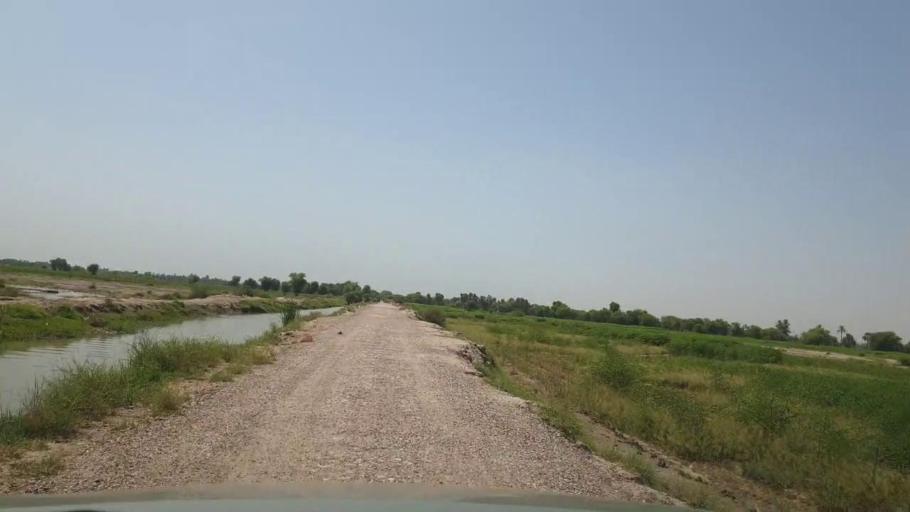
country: PK
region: Sindh
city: Rohri
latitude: 27.6609
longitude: 68.9814
